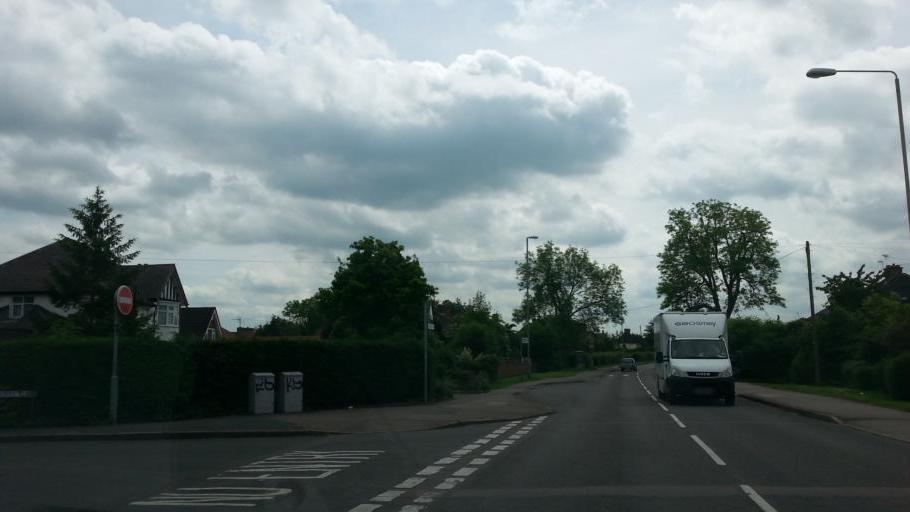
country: GB
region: England
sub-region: Leicestershire
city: Blaby
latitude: 52.5718
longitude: -1.1651
